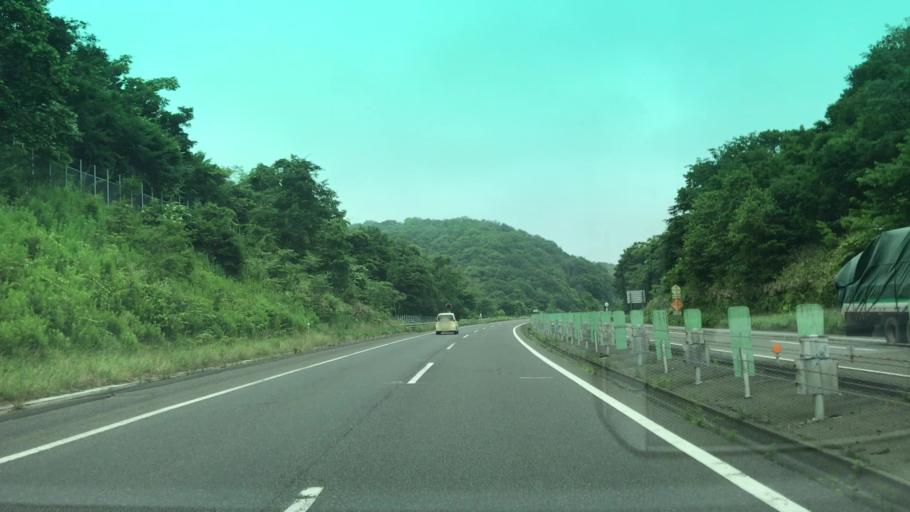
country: JP
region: Hokkaido
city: Shiraoi
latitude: 42.4829
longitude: 141.2234
